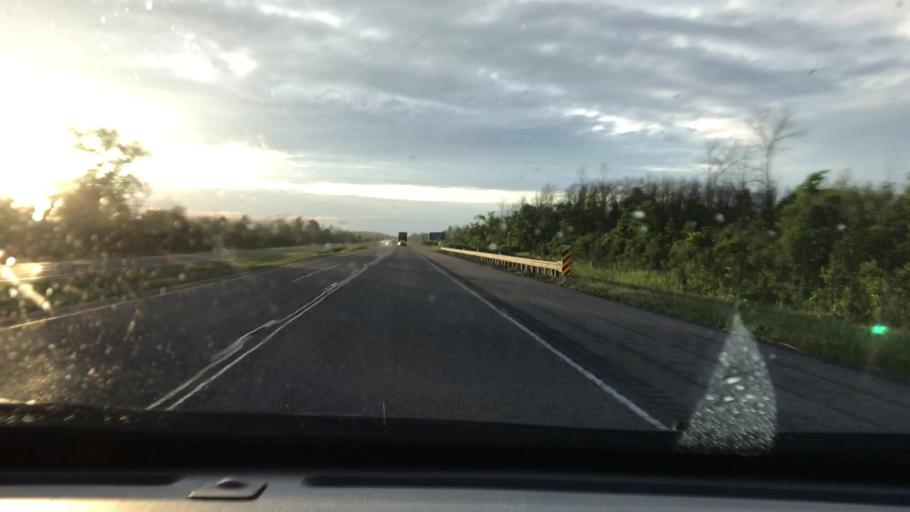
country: US
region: New York
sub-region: Erie County
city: Grandyle Village
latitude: 42.9534
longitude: -79.0085
